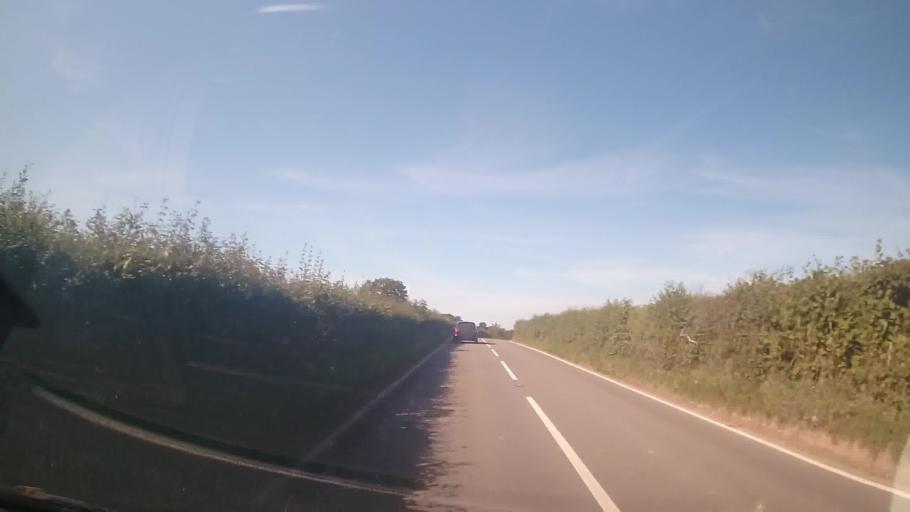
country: GB
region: England
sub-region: Shropshire
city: Lydham
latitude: 52.5201
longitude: -2.9880
